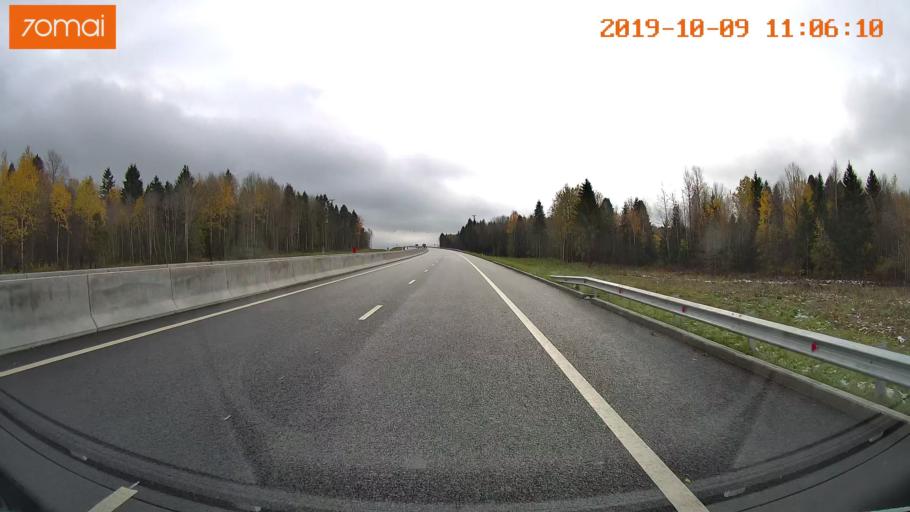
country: RU
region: Vologda
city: Molochnoye
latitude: 59.1900
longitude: 39.7588
